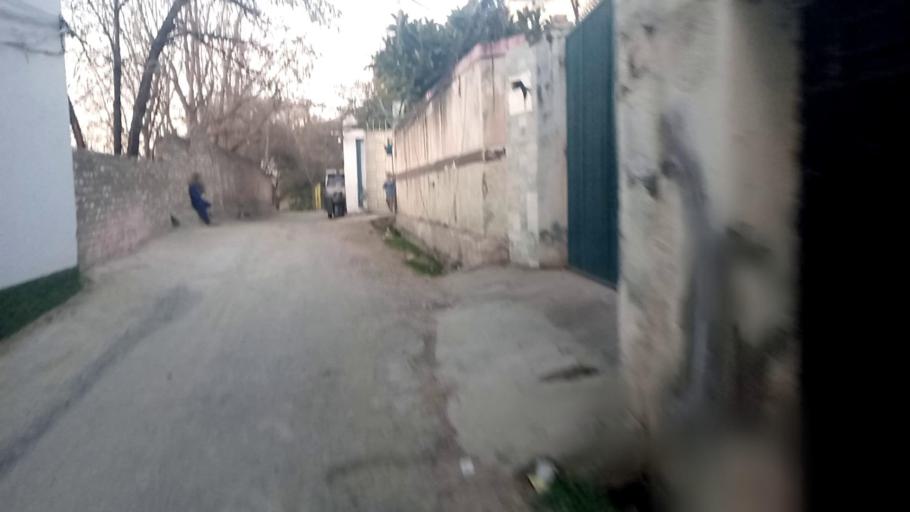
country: PK
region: Khyber Pakhtunkhwa
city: Saidu Sharif
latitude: 34.7546
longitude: 72.3620
